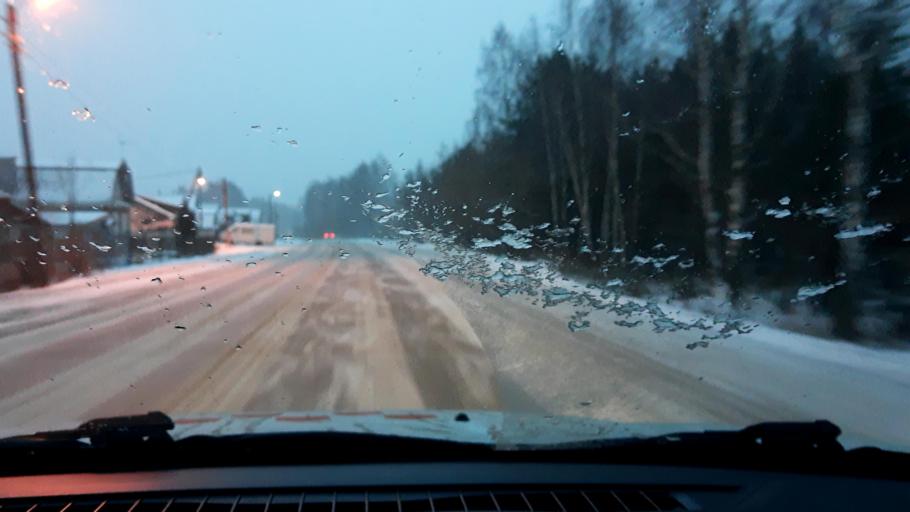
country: RU
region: Nizjnij Novgorod
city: Afonino
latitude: 56.3199
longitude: 44.1555
